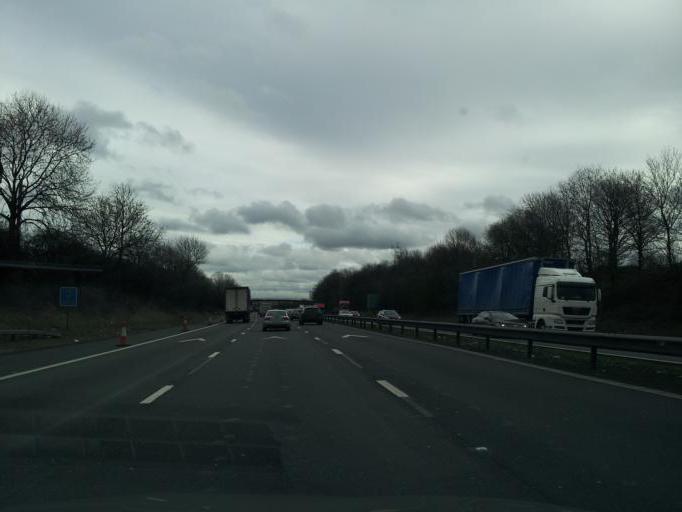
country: GB
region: England
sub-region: Staffordshire
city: Barlaston
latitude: 52.9181
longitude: -2.2008
